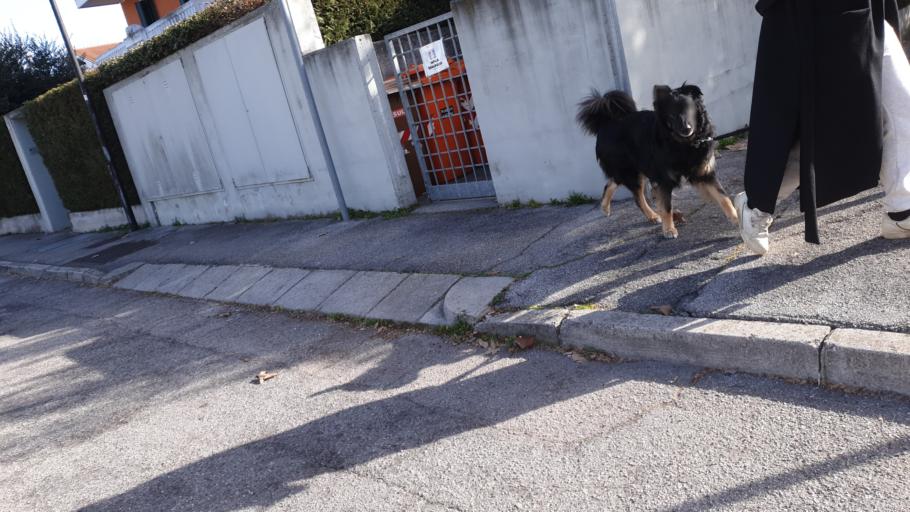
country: IT
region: Veneto
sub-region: Provincia di Padova
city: Noventa
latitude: 45.4176
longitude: 11.9433
